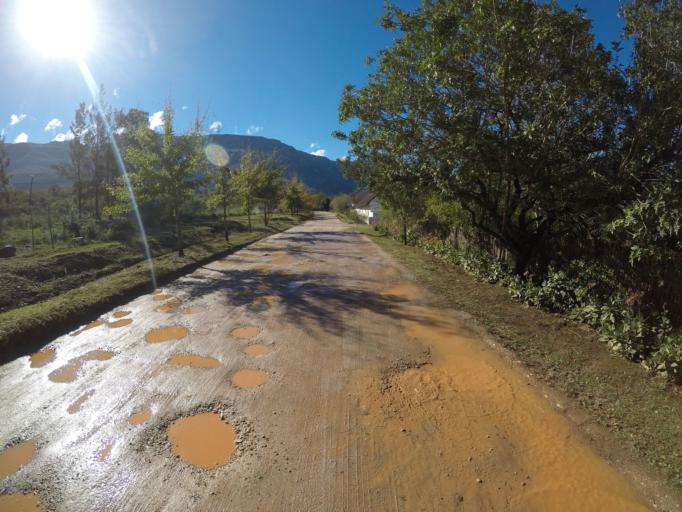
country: ZA
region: Western Cape
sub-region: Overberg District Municipality
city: Caledon
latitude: -34.0474
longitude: 19.6086
